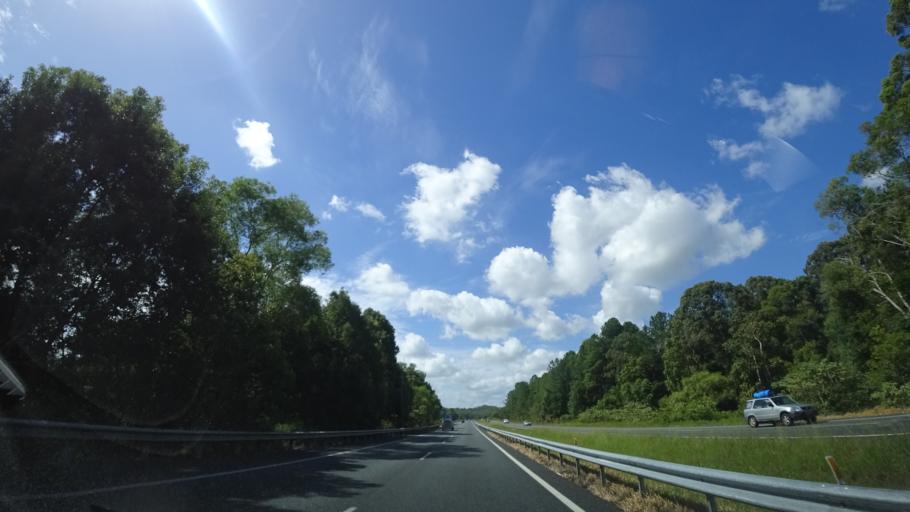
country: AU
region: Queensland
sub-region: Sunshine Coast
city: Woombye
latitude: -26.6487
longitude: 152.9892
